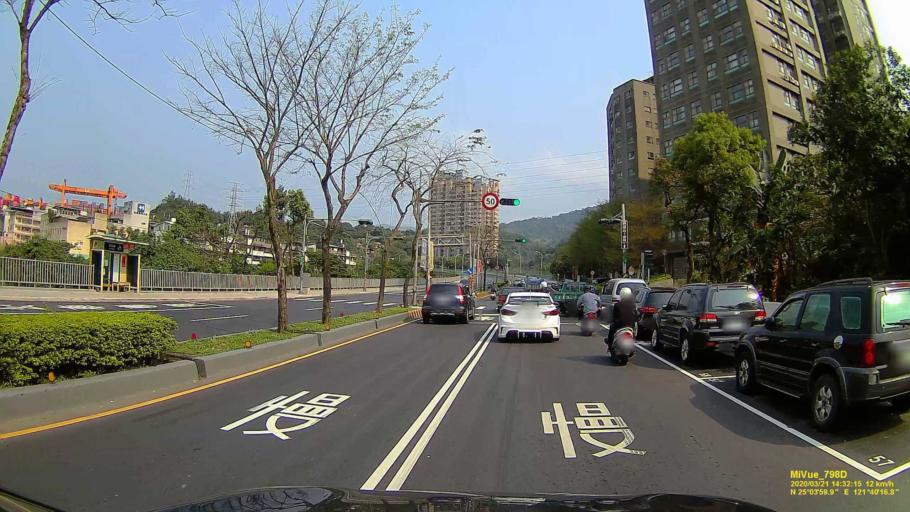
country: TW
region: Taiwan
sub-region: Keelung
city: Keelung
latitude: 25.0665
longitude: 121.6713
